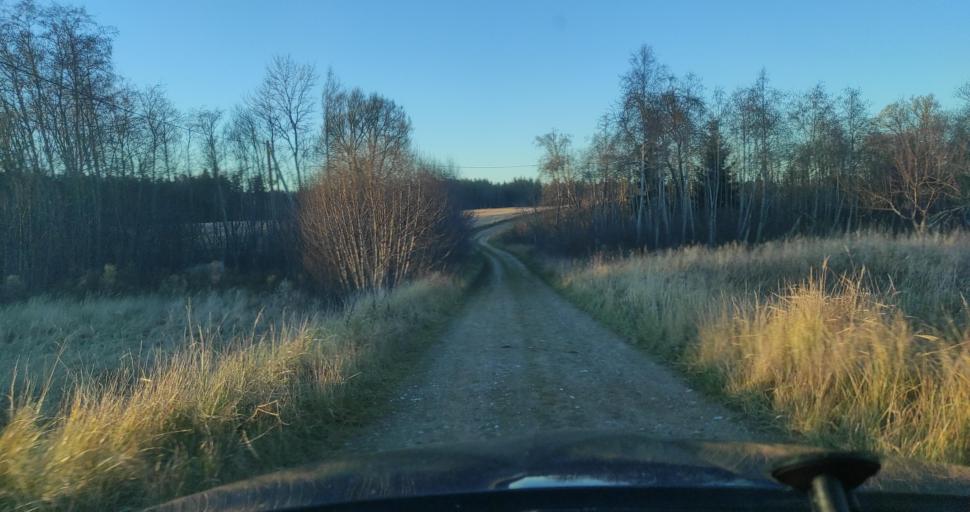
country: LV
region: Dundaga
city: Dundaga
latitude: 57.3912
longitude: 22.0884
